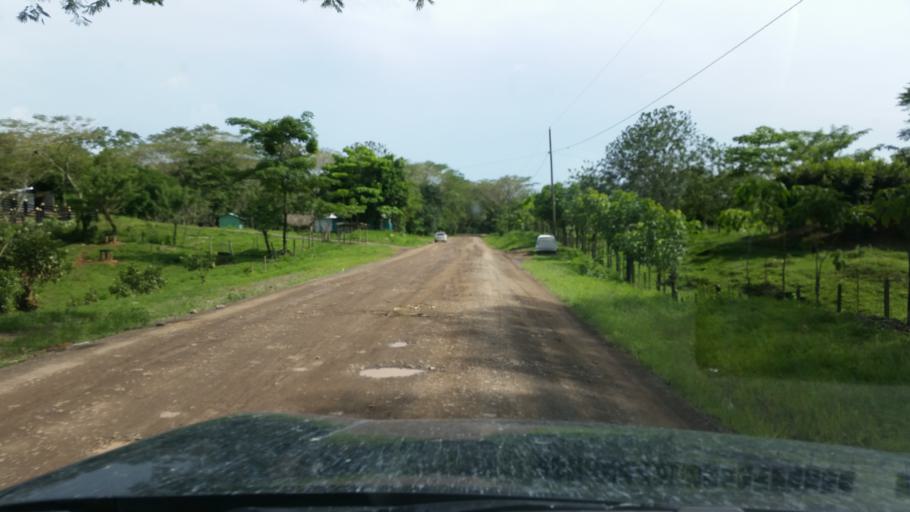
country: NI
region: Atlantico Norte (RAAN)
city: Siuna
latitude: 13.7073
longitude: -84.7771
